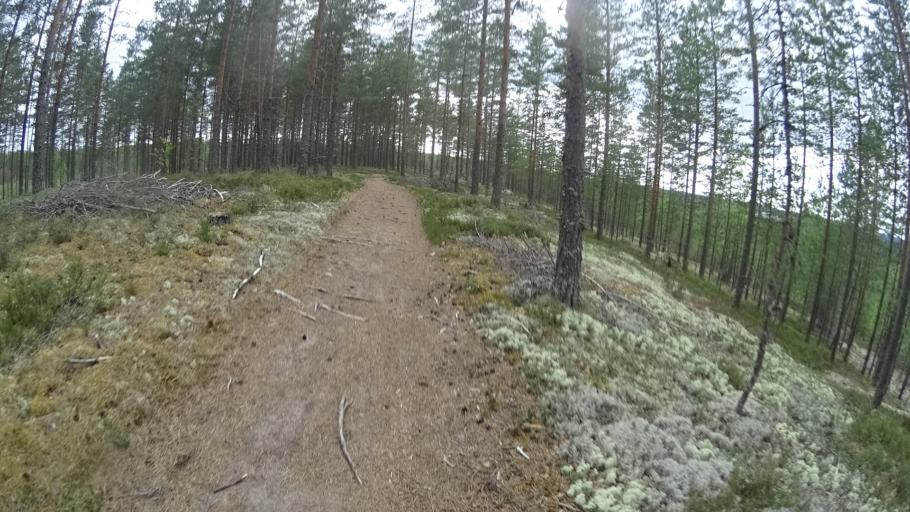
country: FI
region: Satakunta
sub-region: Pohjois-Satakunta
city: Jaemijaervi
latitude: 61.7714
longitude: 22.7994
